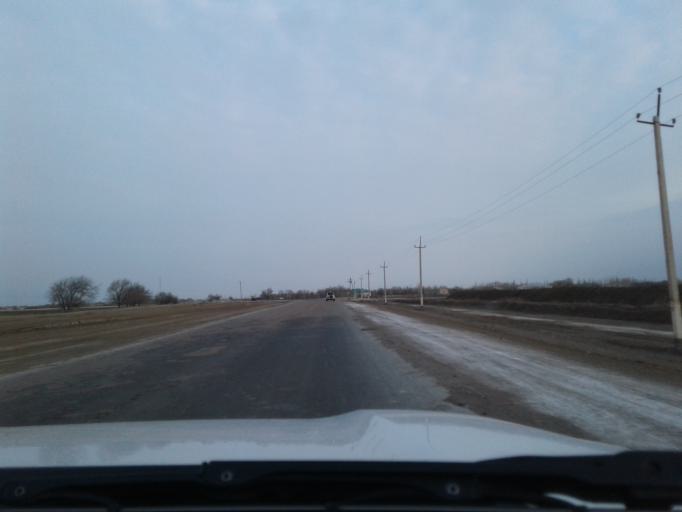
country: TM
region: Dasoguz
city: Boldumsaz
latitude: 42.1642
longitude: 59.5913
